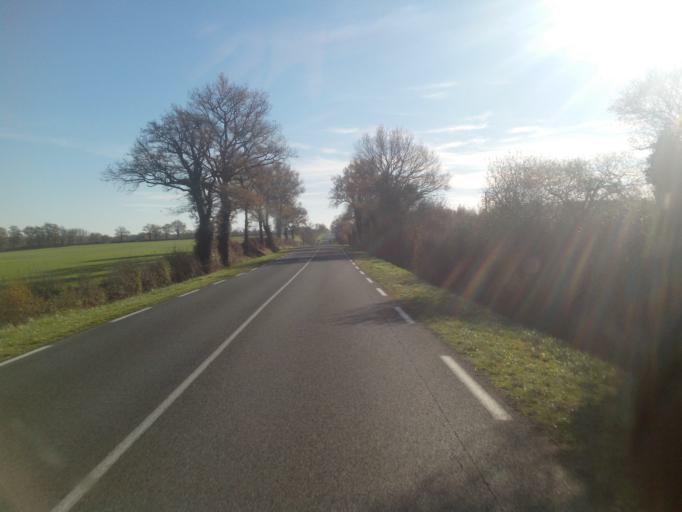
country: FR
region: Limousin
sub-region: Departement de la Haute-Vienne
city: Bussiere-Poitevine
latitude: 46.2954
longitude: 0.8420
